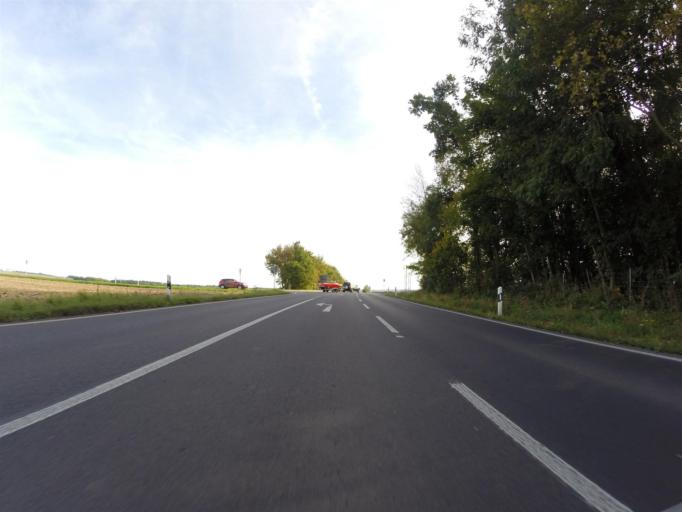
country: DE
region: Thuringia
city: Kapellendorf
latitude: 50.9713
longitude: 11.5228
